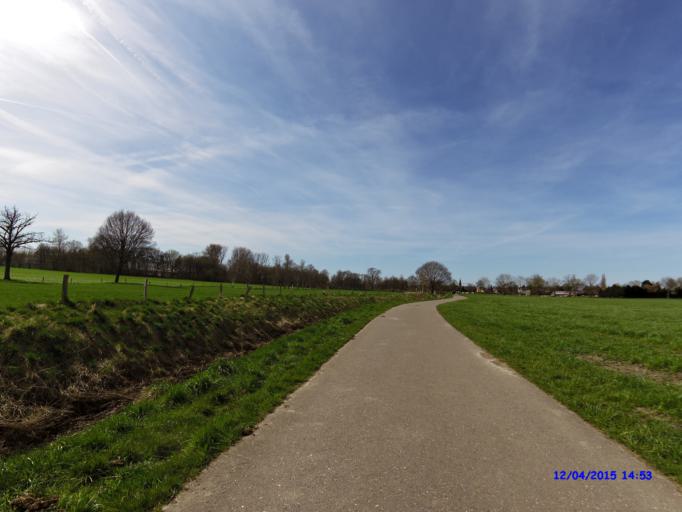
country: DE
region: North Rhine-Westphalia
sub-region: Regierungsbezirk Koln
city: Gangelt
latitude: 50.9825
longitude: 6.0455
